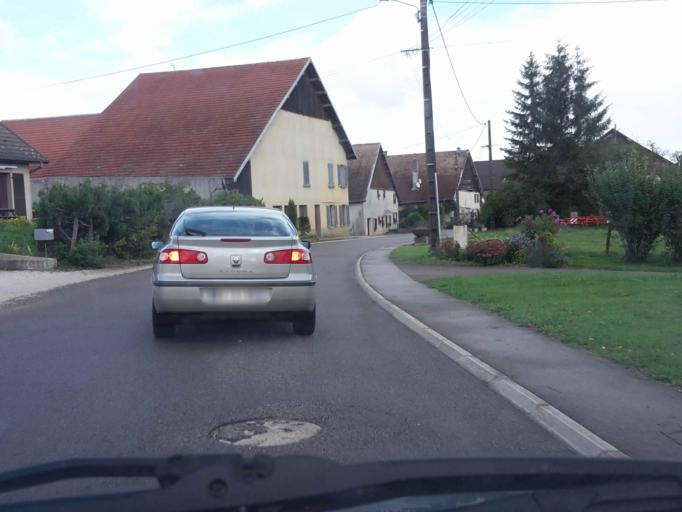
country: FR
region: Franche-Comte
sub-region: Departement du Doubs
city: Nancray
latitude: 47.2659
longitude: 6.2110
